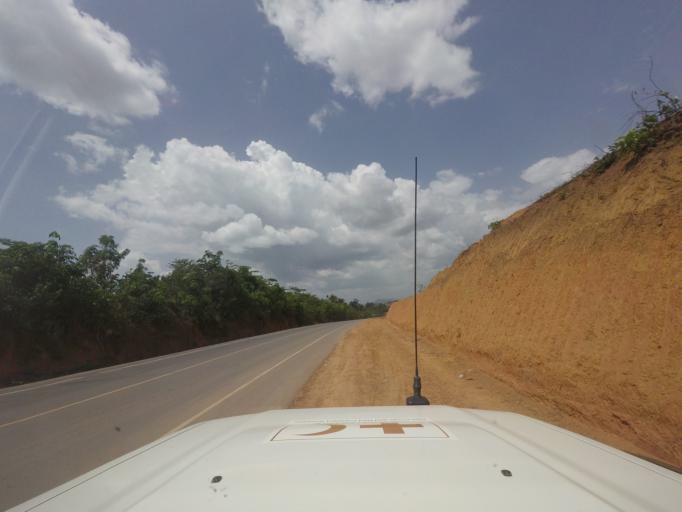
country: LR
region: Nimba
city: Sanniquellie
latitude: 7.2152
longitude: -9.0104
